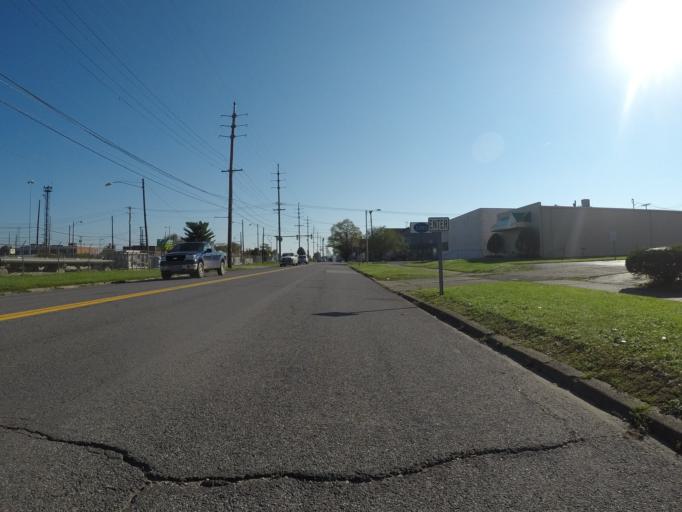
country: US
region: West Virginia
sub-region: Cabell County
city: Huntington
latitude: 38.4151
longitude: -82.4415
